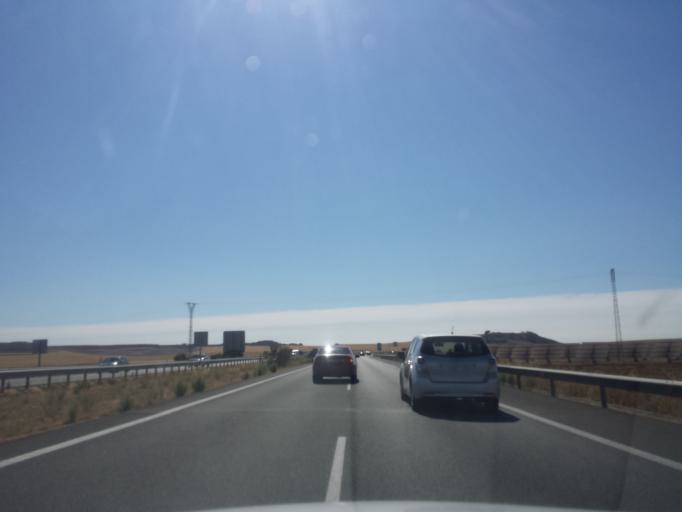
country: ES
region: Castille and Leon
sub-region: Provincia de Valladolid
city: Mota del Marques
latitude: 41.6248
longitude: -5.1698
